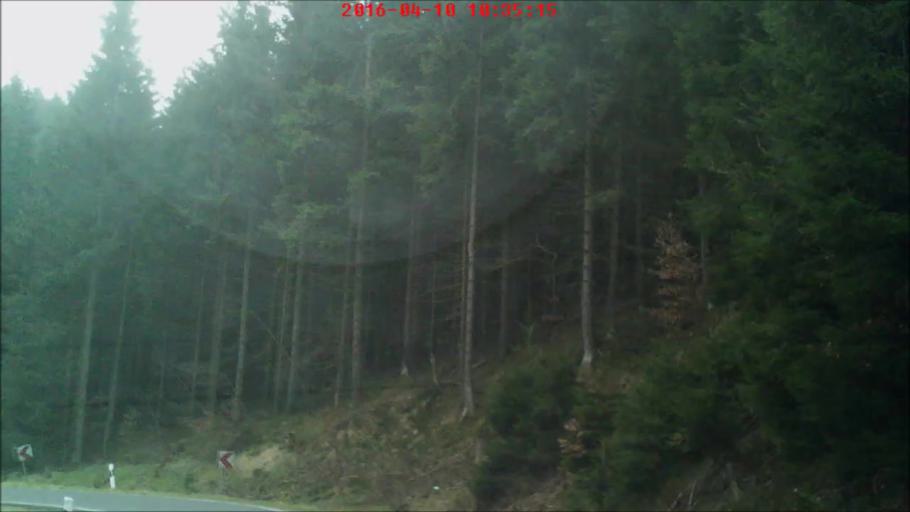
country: DE
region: Thuringia
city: Stutzerbach
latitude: 50.6130
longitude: 10.8646
